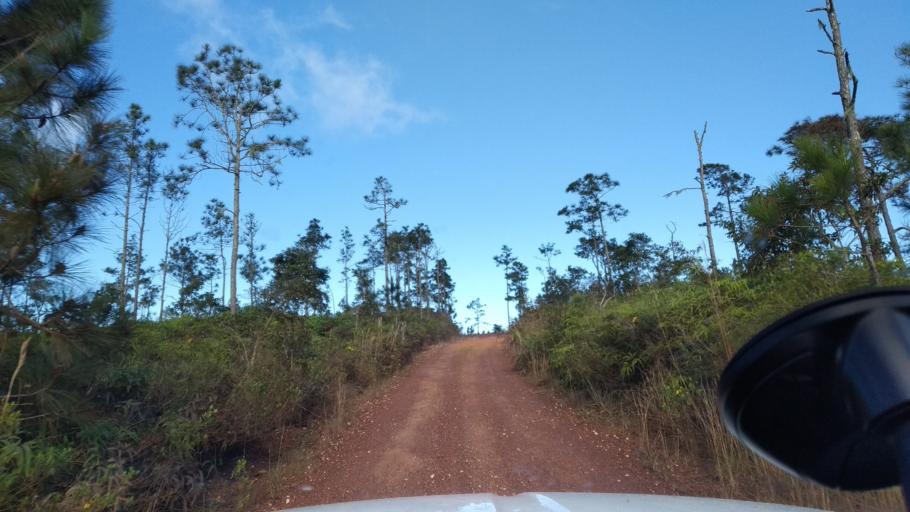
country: BZ
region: Cayo
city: Belmopan
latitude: 16.9976
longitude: -88.8387
